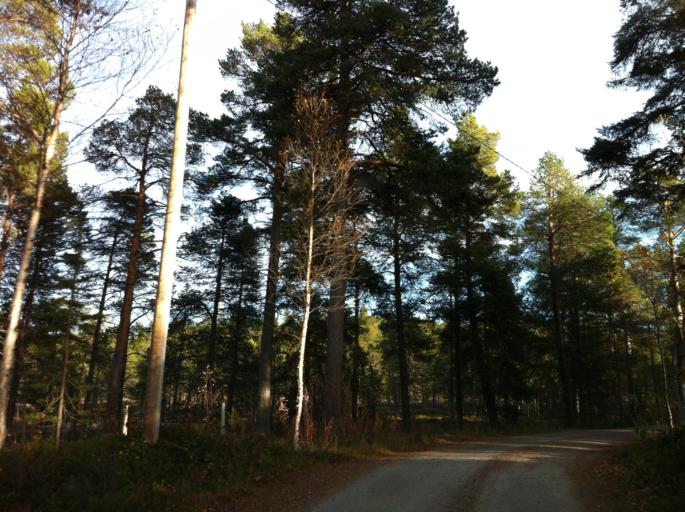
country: NO
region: Hedmark
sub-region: Engerdal
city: Engerdal
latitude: 62.1711
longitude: 11.9426
